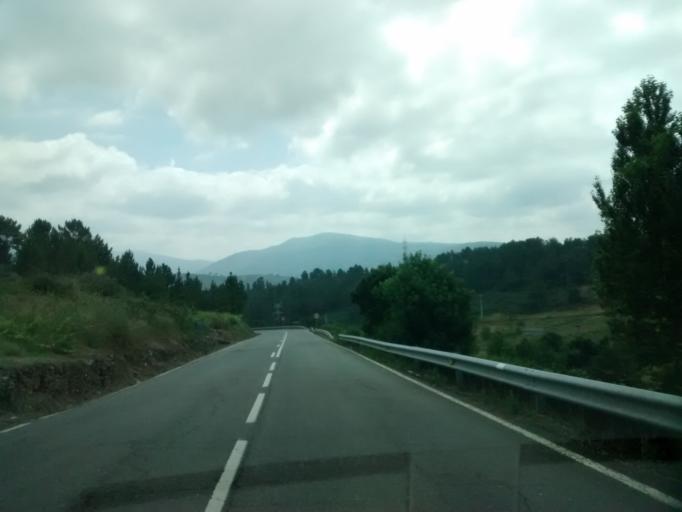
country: ES
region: Galicia
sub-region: Provincia de Ourense
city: Petin
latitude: 42.3495
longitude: -7.1581
